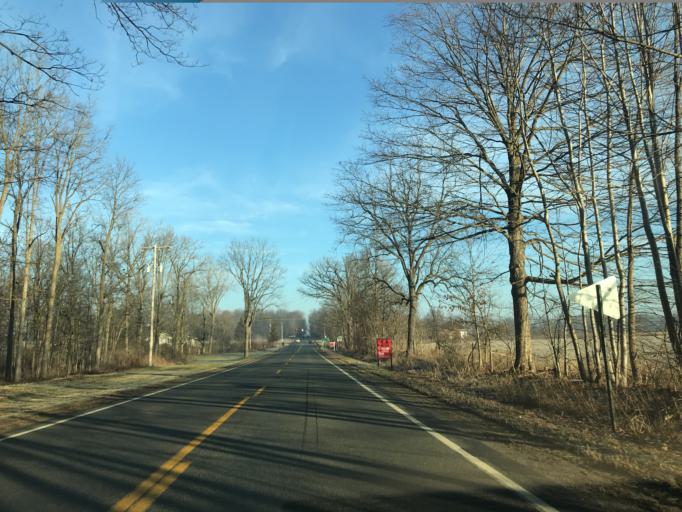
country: US
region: Michigan
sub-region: Eaton County
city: Dimondale
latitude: 42.6377
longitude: -84.6029
